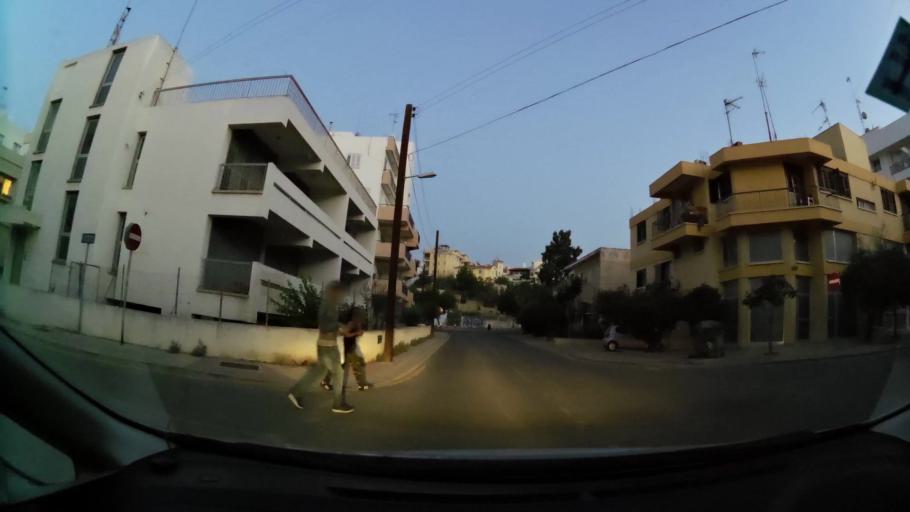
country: CY
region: Lefkosia
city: Nicosia
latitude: 35.1630
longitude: 33.3693
